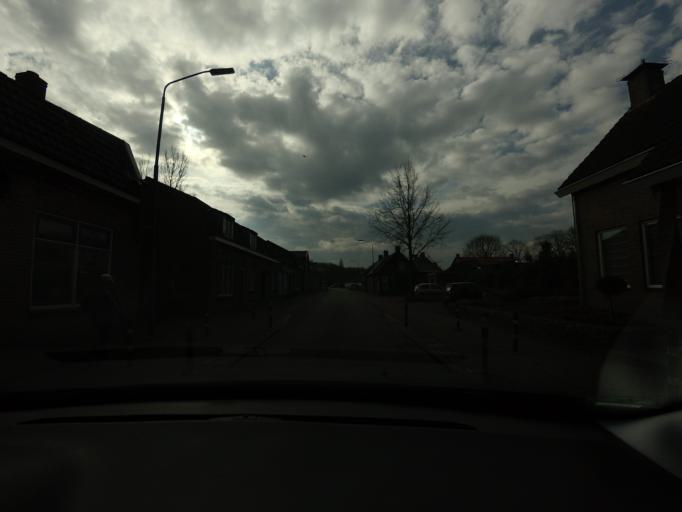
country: NL
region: North Brabant
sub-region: Gemeente Waalwijk
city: Waspik
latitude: 51.6800
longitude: 4.9479
